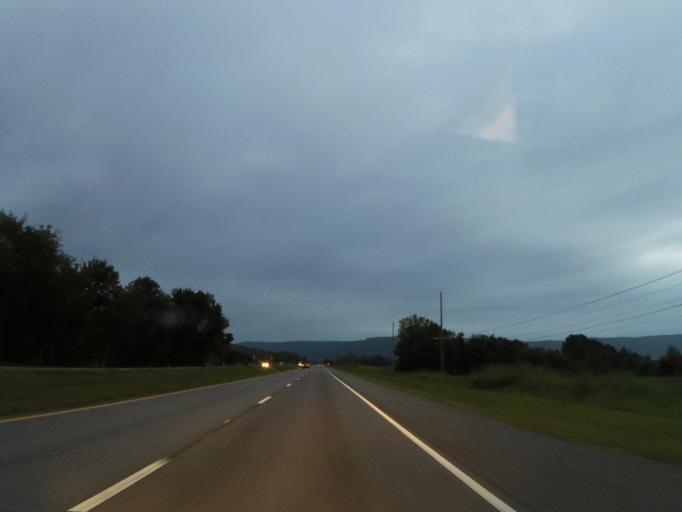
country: US
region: Alabama
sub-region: Madison County
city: Owens Cross Roads
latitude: 34.7185
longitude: -86.4092
